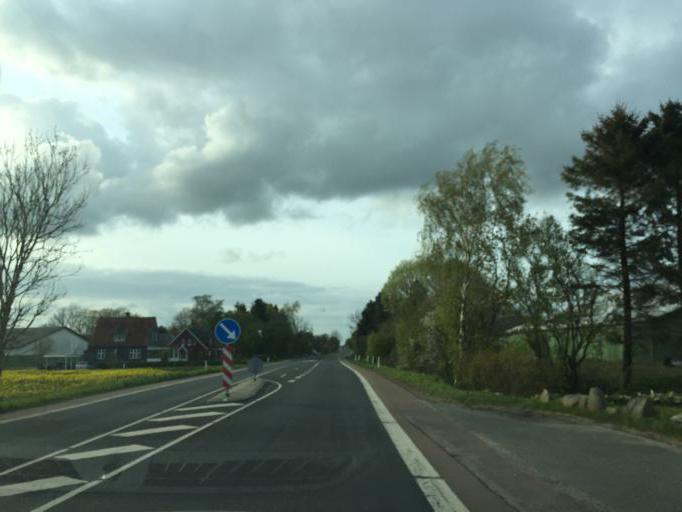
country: DK
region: South Denmark
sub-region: Svendborg Kommune
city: Svendborg
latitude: 55.1255
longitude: 10.5576
